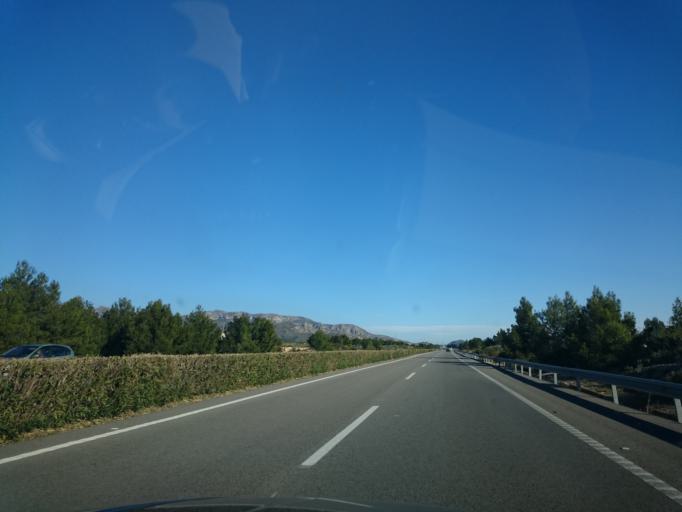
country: ES
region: Catalonia
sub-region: Provincia de Tarragona
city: l'Ametlla de Mar
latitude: 40.9178
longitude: 0.8300
